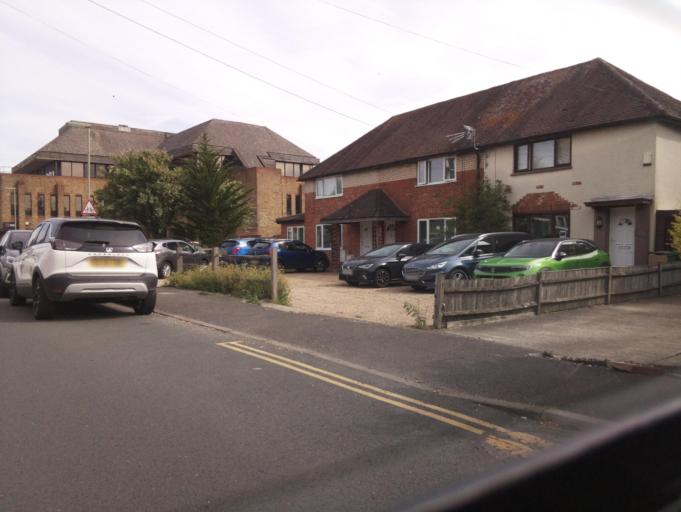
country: GB
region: England
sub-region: Surrey
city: Horley
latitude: 51.1726
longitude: -0.1603
